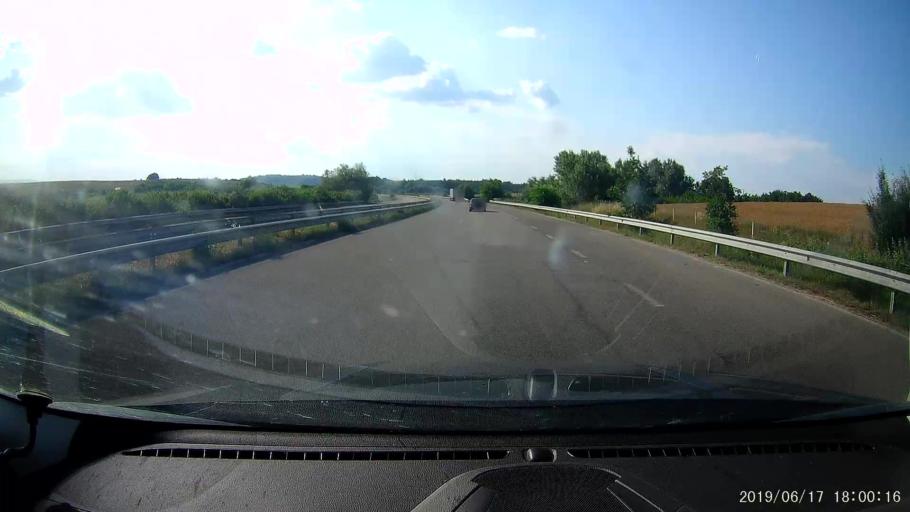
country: BG
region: Khaskovo
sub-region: Obshtina Svilengrad
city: Svilengrad
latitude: 41.7342
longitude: 26.2820
